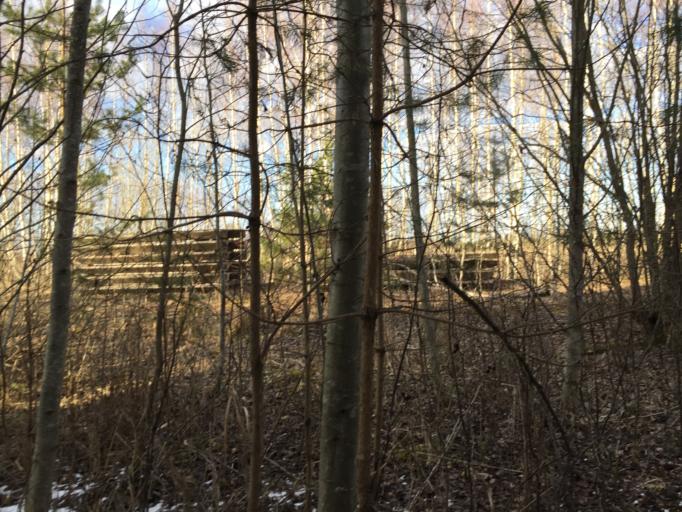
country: LV
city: Tireli
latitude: 56.8727
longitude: 23.6150
